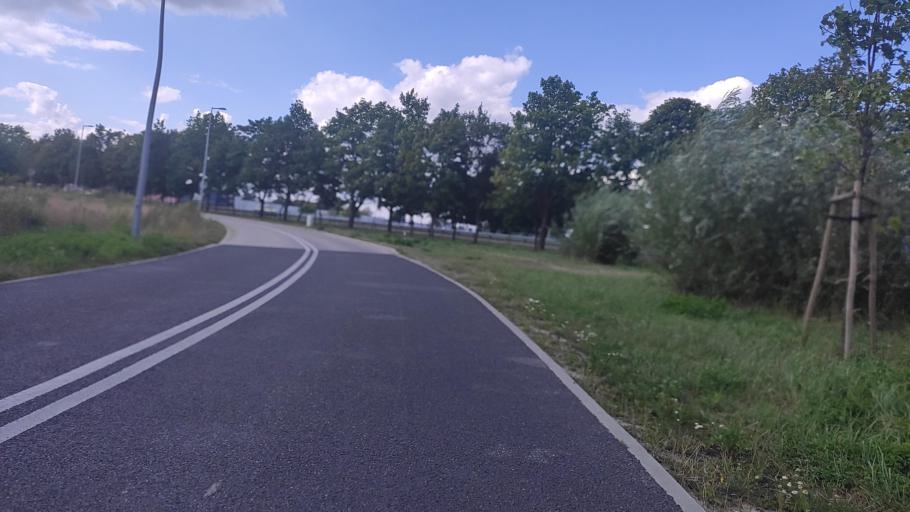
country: PL
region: Greater Poland Voivodeship
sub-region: Powiat poznanski
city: Swarzedz
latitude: 52.4024
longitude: 17.1208
